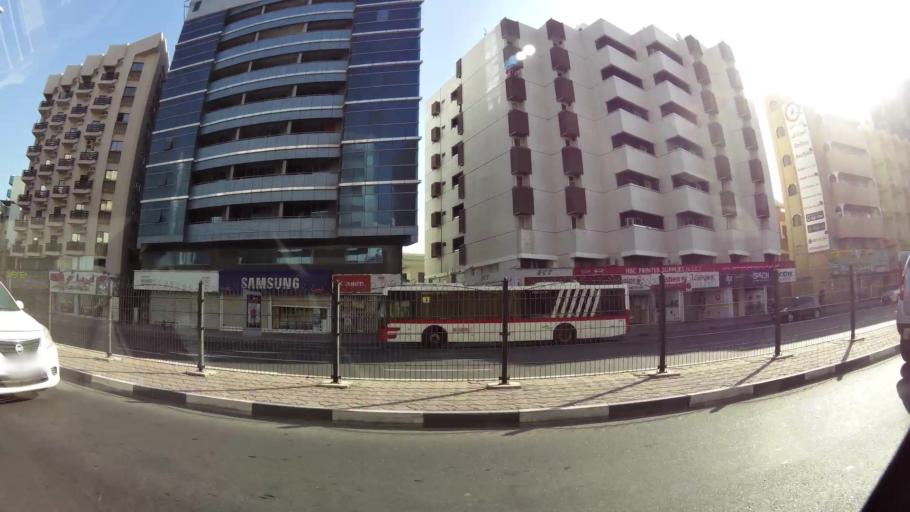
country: AE
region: Ash Shariqah
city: Sharjah
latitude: 25.2602
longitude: 55.2859
